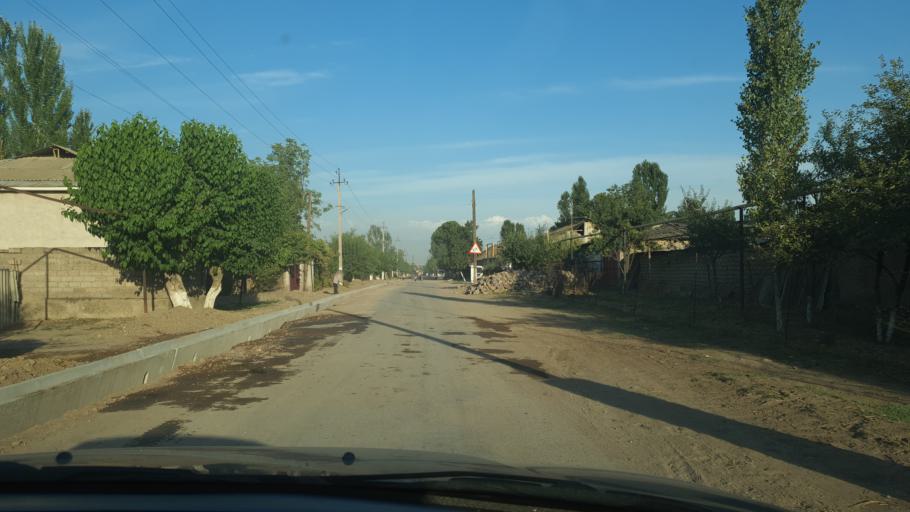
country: UZ
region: Toshkent
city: Tuytepa
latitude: 41.1048
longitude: 69.3975
